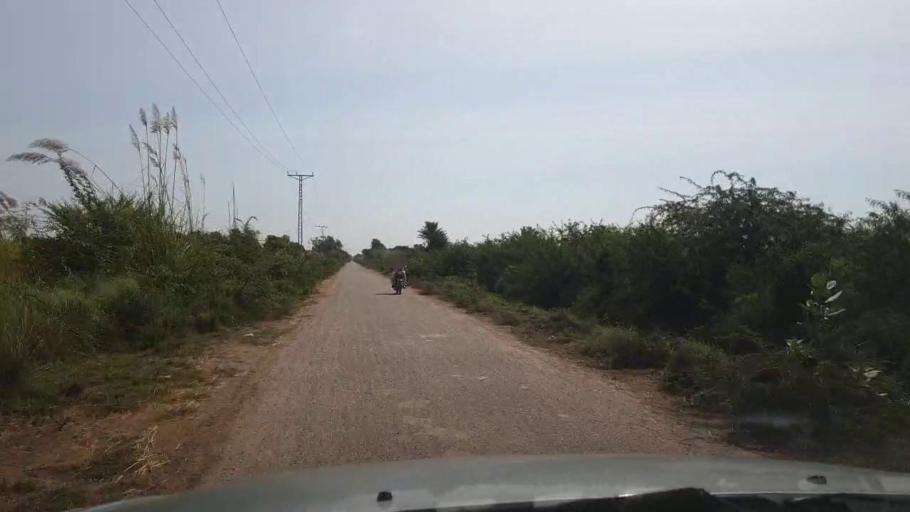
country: PK
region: Sindh
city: Tando Muhammad Khan
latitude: 25.1550
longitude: 68.3815
